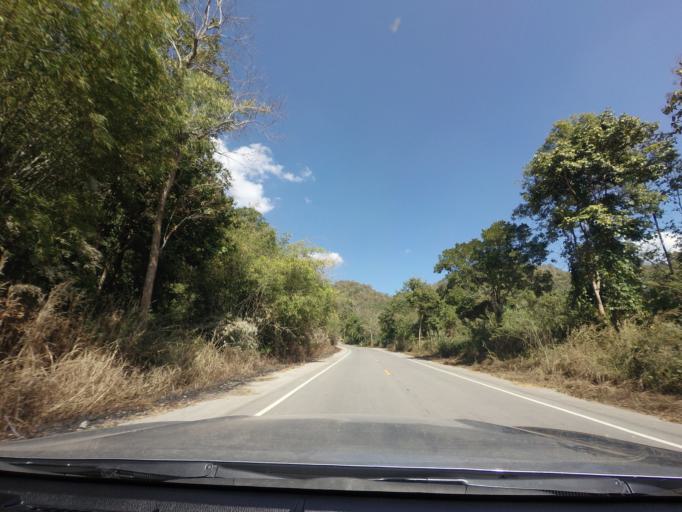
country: TH
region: Lampang
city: Chae Hom
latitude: 18.5556
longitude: 99.6261
